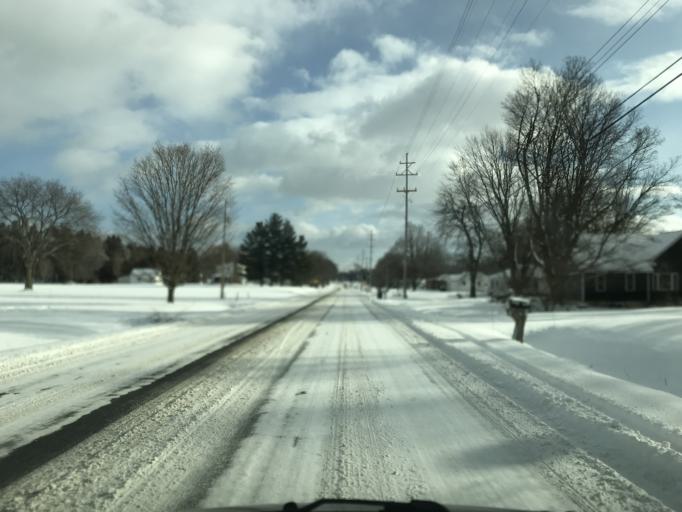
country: US
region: Michigan
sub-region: Kent County
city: Byron Center
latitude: 42.8266
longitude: -85.7083
